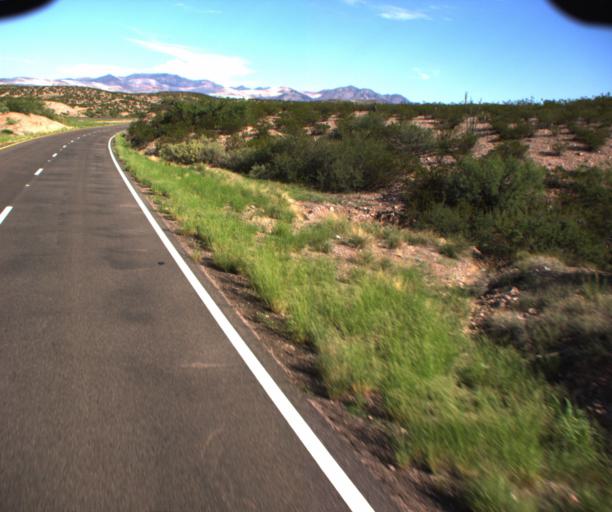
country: US
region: Arizona
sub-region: Greenlee County
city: Clifton
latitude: 32.9930
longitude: -109.2716
